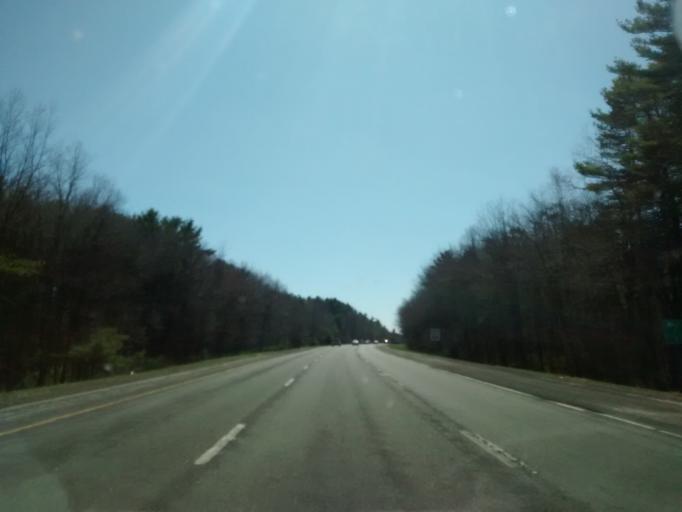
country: US
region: Massachusetts
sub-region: Hampden County
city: Holland
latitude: 42.0454
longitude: -72.1241
